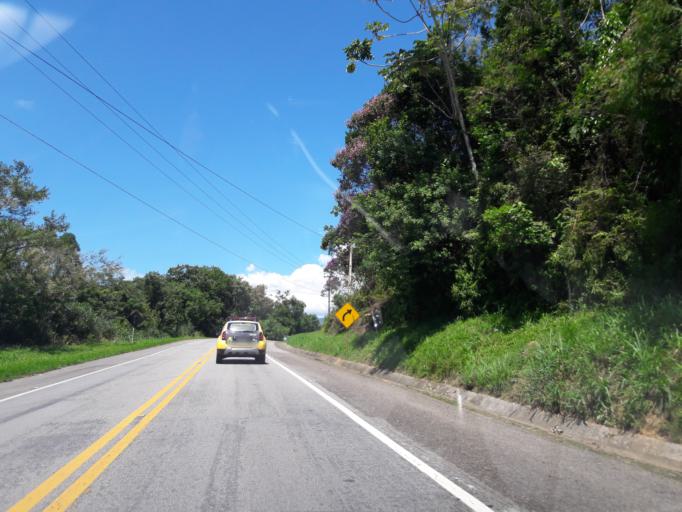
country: BR
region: Parana
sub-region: Antonina
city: Antonina
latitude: -25.5161
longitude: -48.8051
